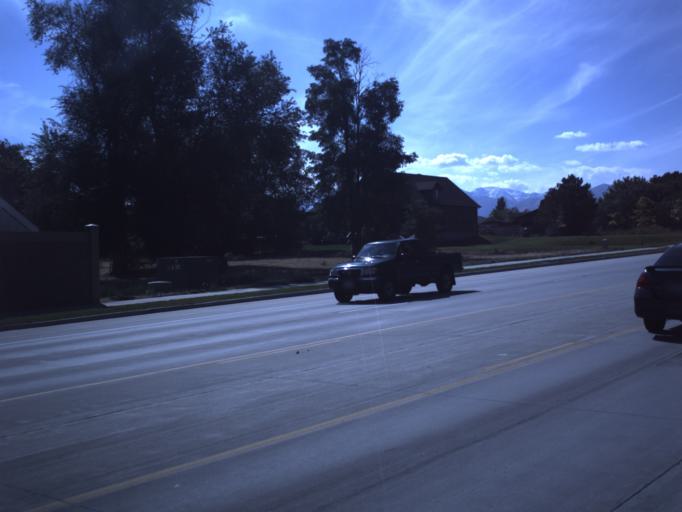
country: US
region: Utah
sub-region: Salt Lake County
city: South Jordan Heights
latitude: 40.5623
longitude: -111.9642
